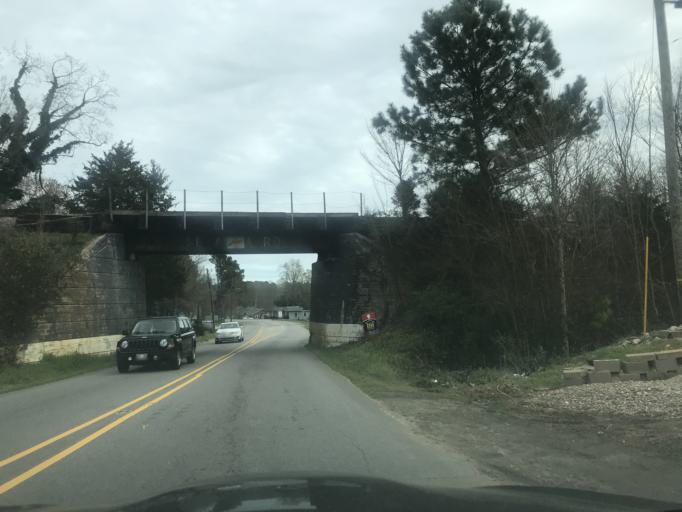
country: US
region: North Carolina
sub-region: Franklin County
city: Franklinton
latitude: 36.1016
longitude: -78.4572
